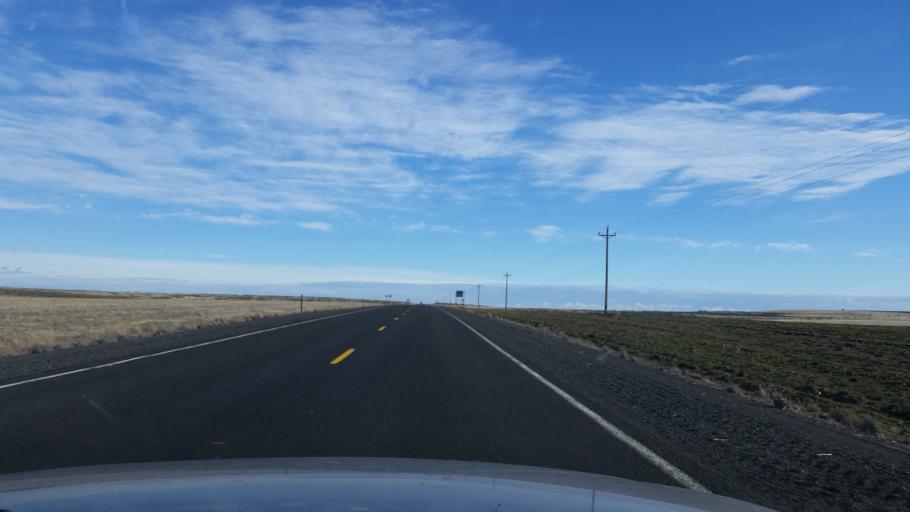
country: US
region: Washington
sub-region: Grant County
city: Warden
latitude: 47.3158
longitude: -118.8130
